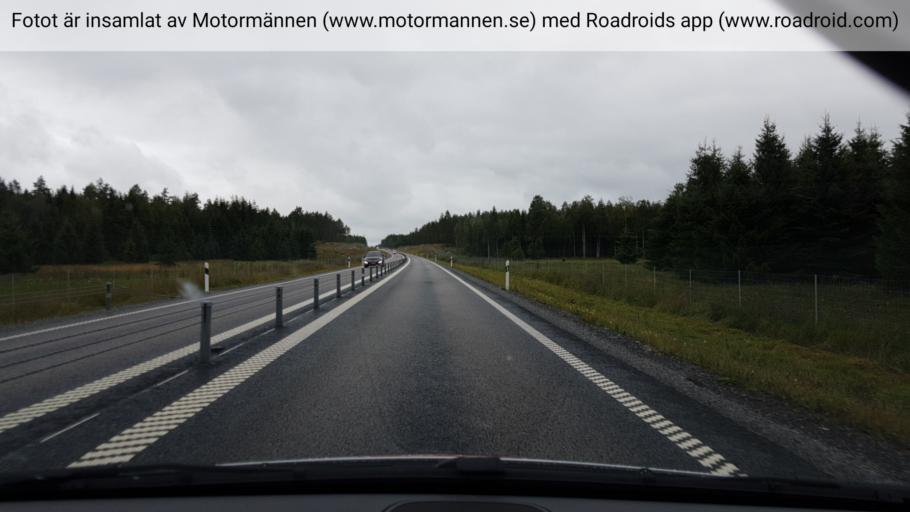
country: SE
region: Uppsala
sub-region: Heby Kommun
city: Tarnsjo
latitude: 60.0839
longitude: 16.9166
